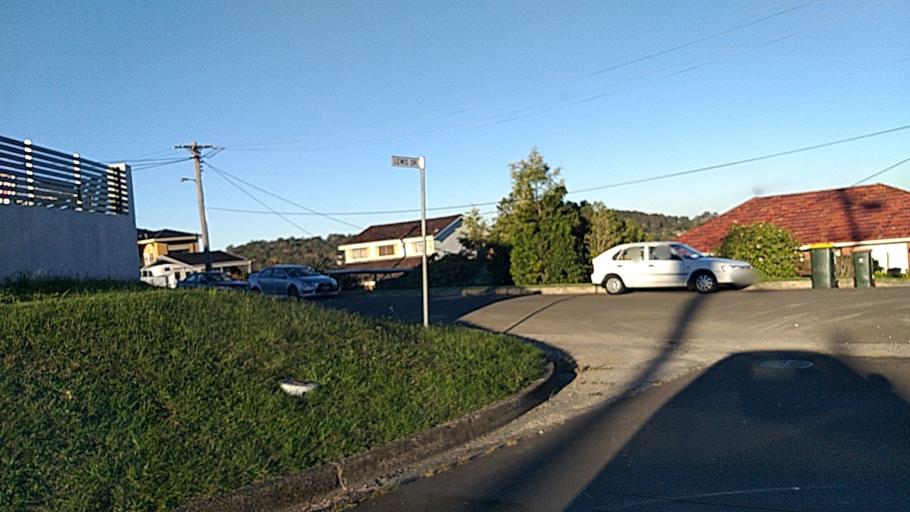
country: AU
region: New South Wales
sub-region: Wollongong
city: West Wollongong
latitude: -34.4326
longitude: 150.8576
